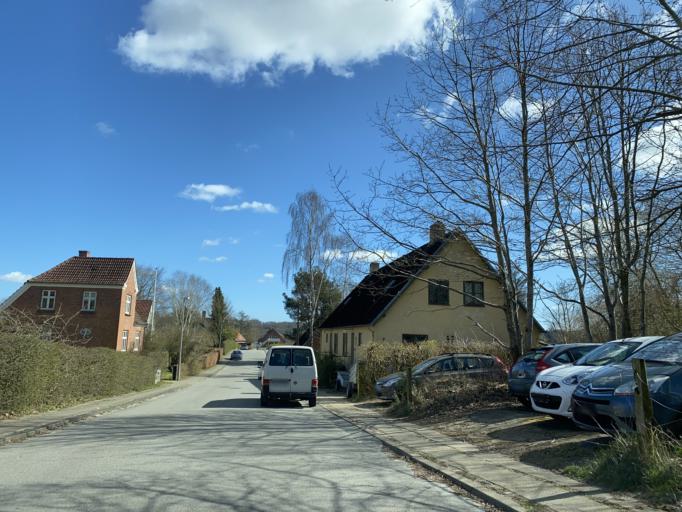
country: DK
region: Central Jutland
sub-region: Randers Kommune
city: Langa
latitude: 56.3861
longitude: 9.8903
